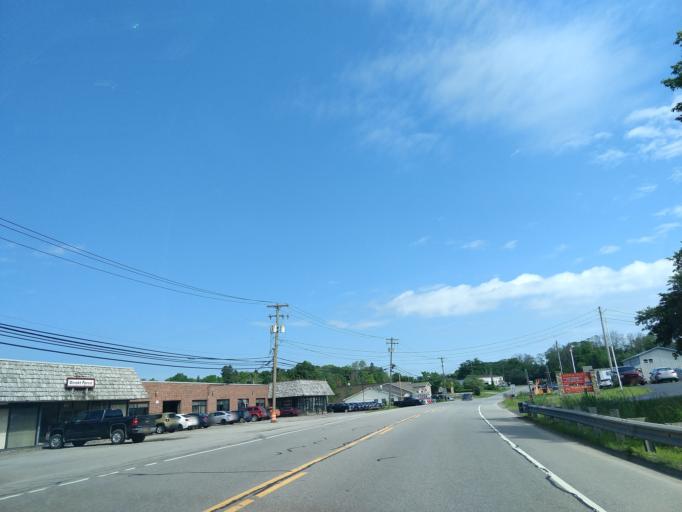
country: US
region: New York
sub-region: Erie County
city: East Aurora
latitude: 42.7542
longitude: -78.6079
